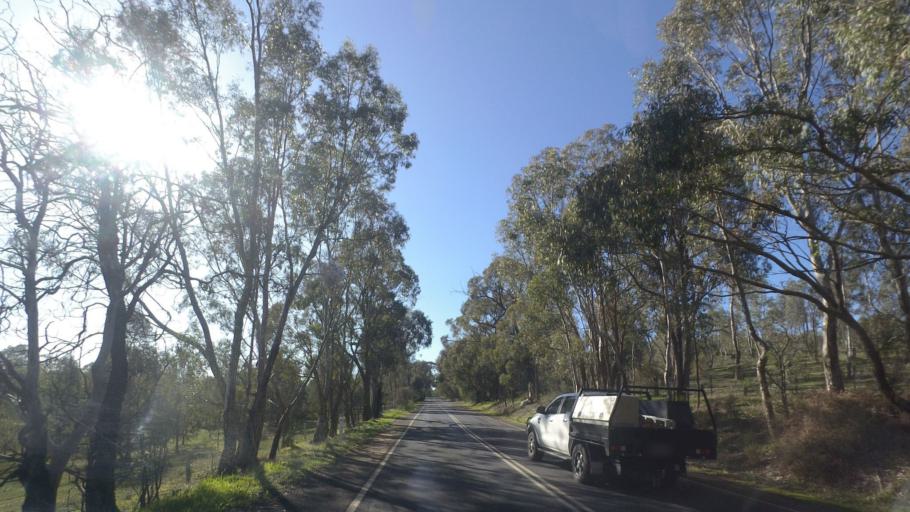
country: AU
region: Victoria
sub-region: Greater Bendigo
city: Kennington
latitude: -36.9424
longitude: 144.3391
